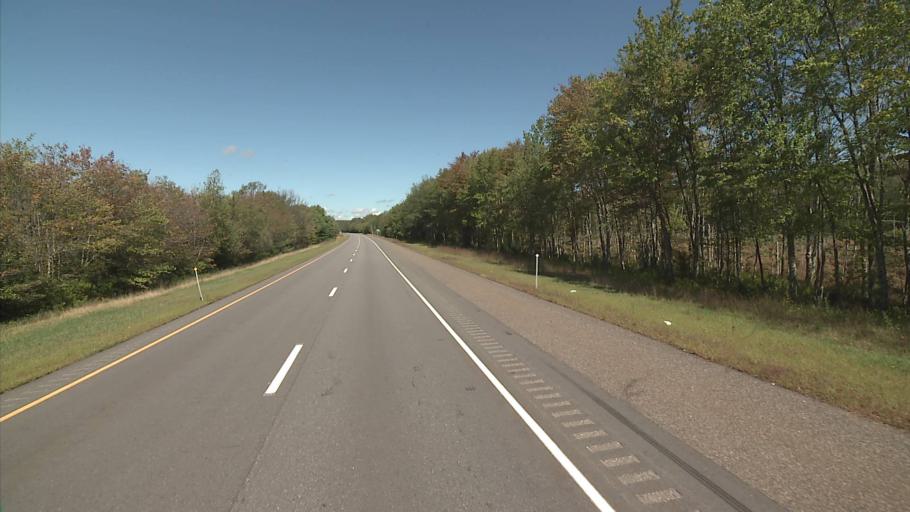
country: US
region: Connecticut
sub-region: New London County
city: Colchester
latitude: 41.5187
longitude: -72.3030
